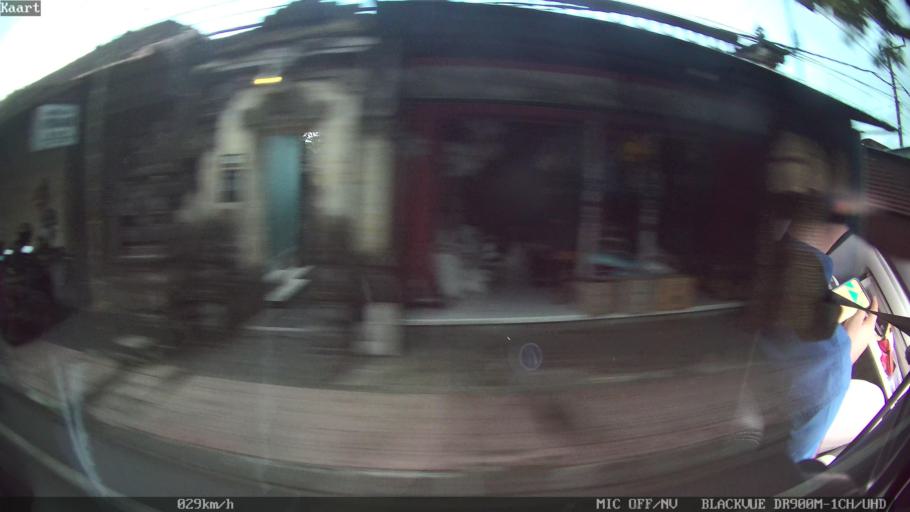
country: ID
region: Bali
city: Bunutan
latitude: -8.4783
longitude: 115.2483
